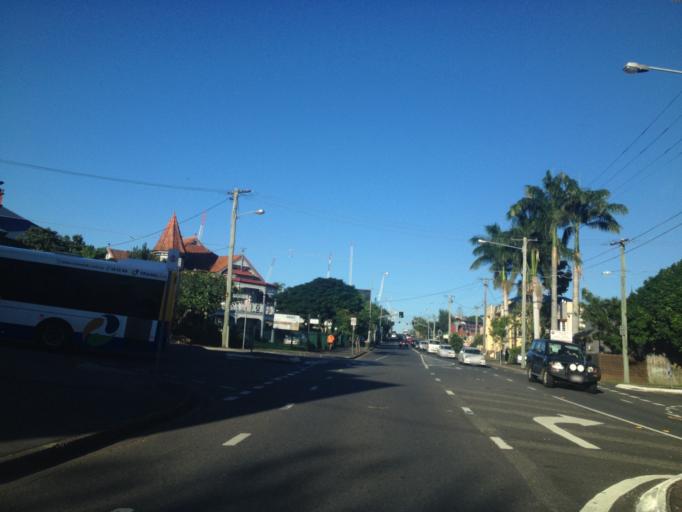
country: AU
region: Queensland
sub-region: Brisbane
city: South Brisbane
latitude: -27.4814
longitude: 153.0152
